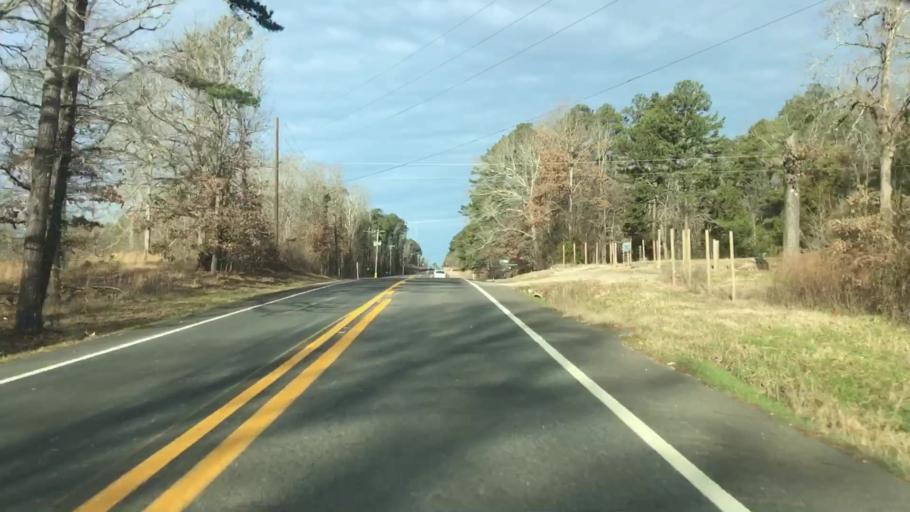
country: US
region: Arkansas
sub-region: Montgomery County
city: Mount Ida
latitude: 34.5403
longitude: -93.6059
